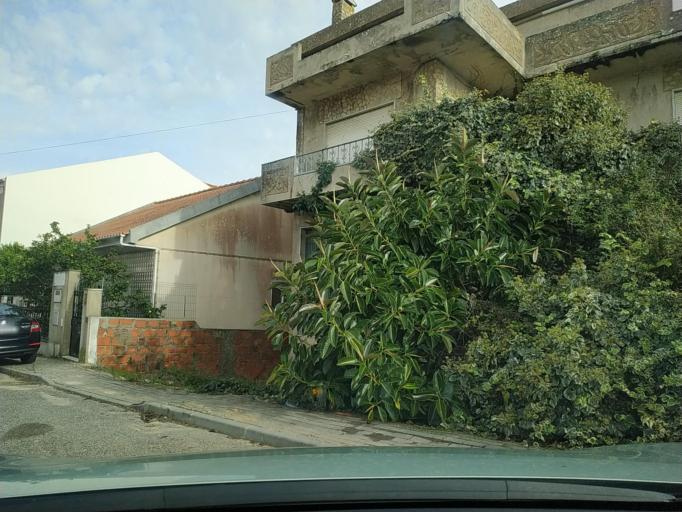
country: PT
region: Lisbon
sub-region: Sintra
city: Belas
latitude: 38.7772
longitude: -9.2437
